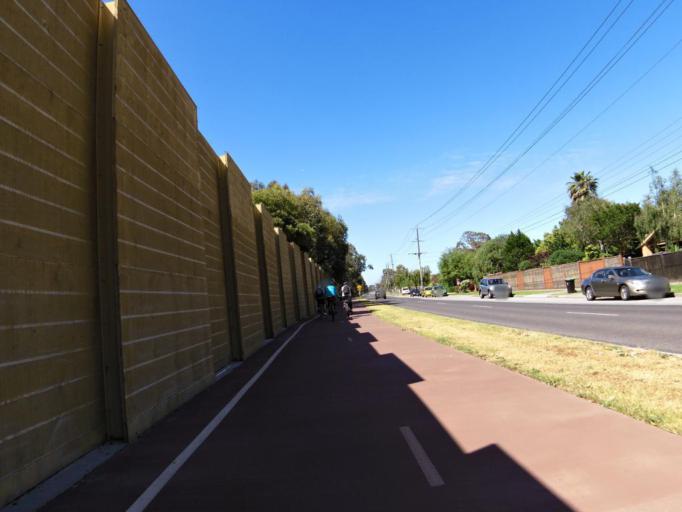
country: AU
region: Victoria
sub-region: Kingston
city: Patterson Lakes
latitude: -38.0735
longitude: 145.1498
